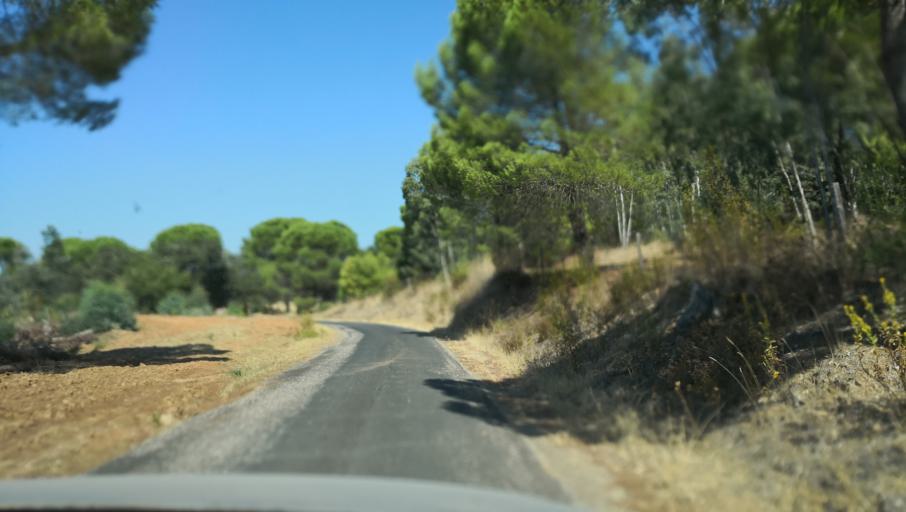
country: PT
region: Setubal
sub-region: Alcacer do Sal
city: Alcacer do Sal
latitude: 38.2523
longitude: -8.2980
